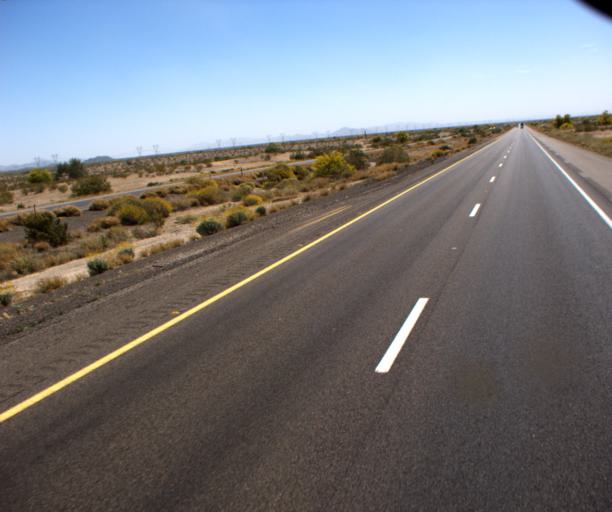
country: US
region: Arizona
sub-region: Maricopa County
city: Gila Bend
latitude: 33.0834
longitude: -112.6477
